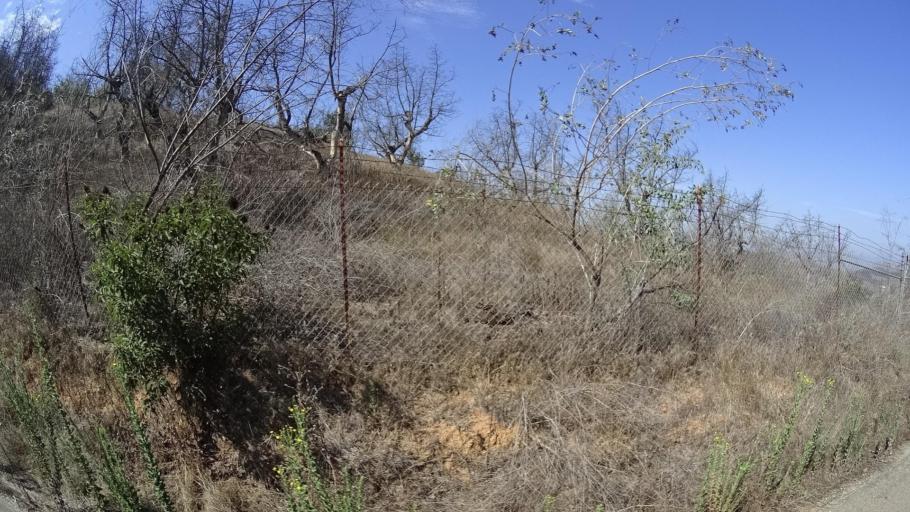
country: US
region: California
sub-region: San Diego County
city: Valley Center
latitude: 33.2985
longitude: -117.0467
